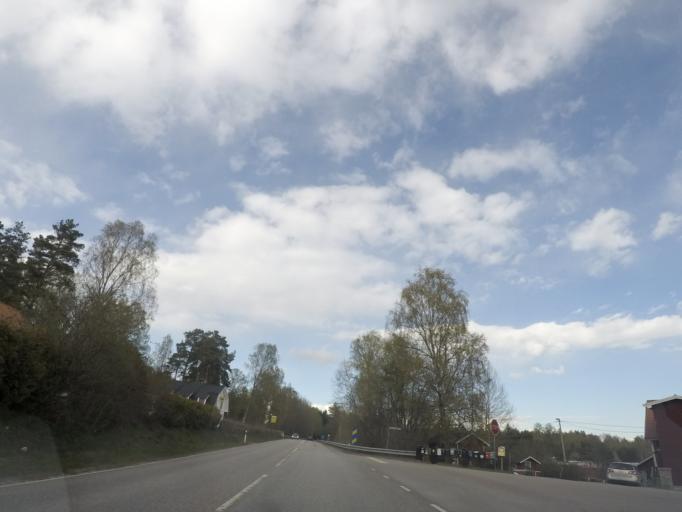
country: SE
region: Soedermanland
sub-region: Eskilstuna Kommun
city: Skogstorp
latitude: 59.3260
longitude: 16.4187
